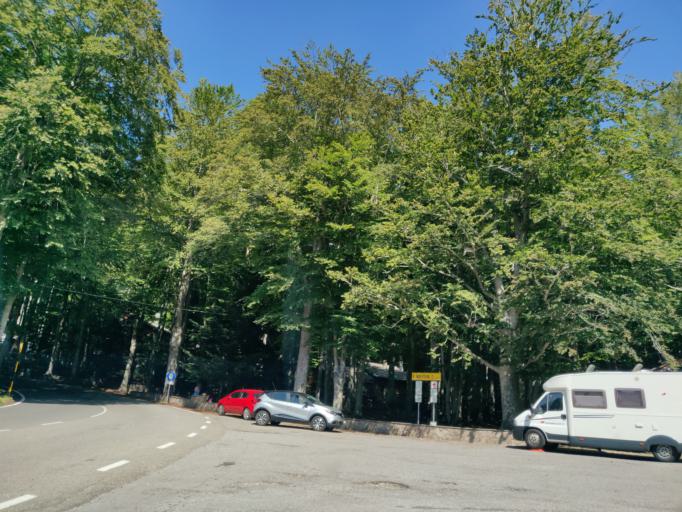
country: IT
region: Tuscany
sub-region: Provincia di Siena
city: Abbadia San Salvatore
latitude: 42.9035
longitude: 11.6344
